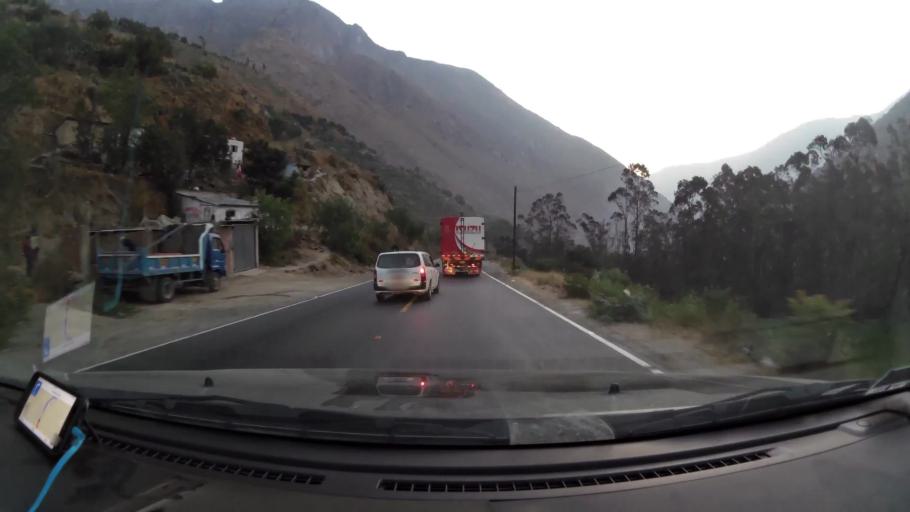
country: PE
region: Lima
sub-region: Provincia de Huarochiri
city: Surco
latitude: -11.8876
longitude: -76.4481
